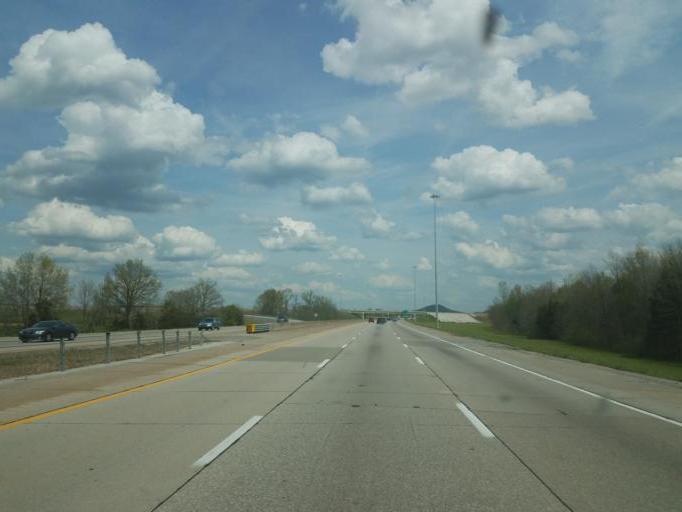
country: US
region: Kentucky
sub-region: Bullitt County
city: Lebanon Junction
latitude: 37.8001
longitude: -85.7510
